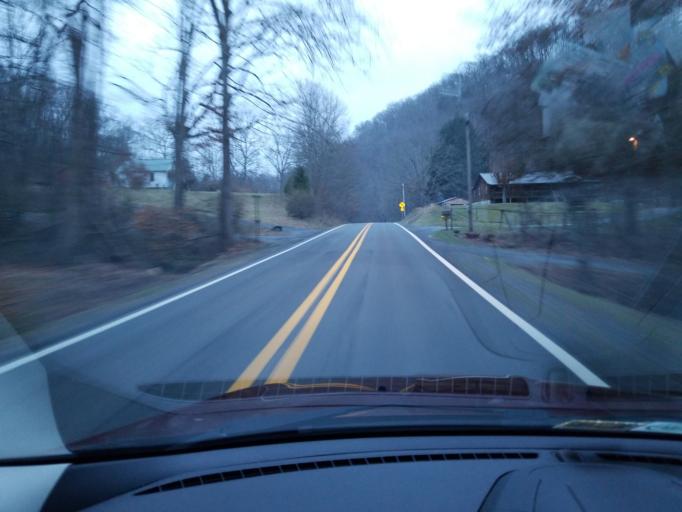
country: US
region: West Virginia
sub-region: Greenbrier County
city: Ronceverte
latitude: 37.7543
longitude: -80.4035
